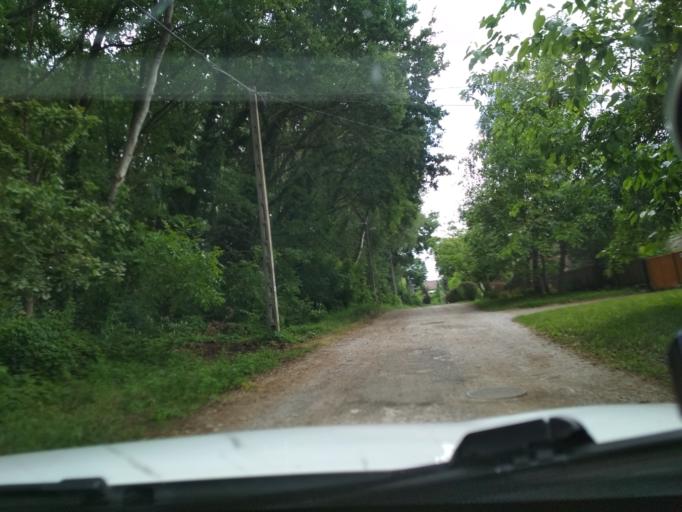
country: HU
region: Jasz-Nagykun-Szolnok
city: Tiszafured
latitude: 47.6203
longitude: 20.7370
